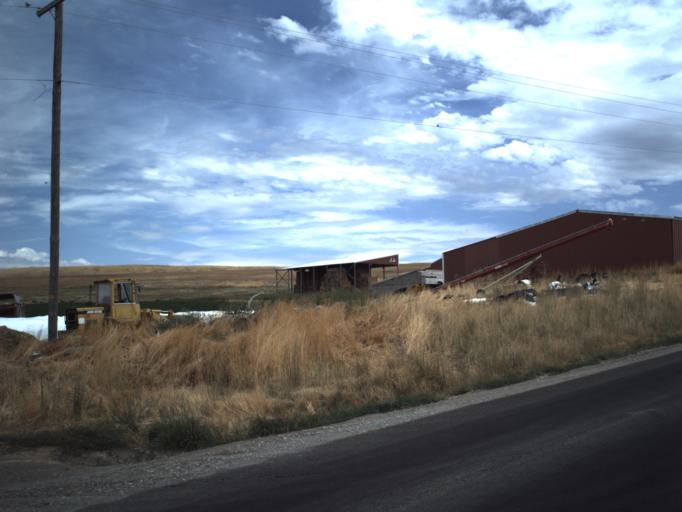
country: US
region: Utah
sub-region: Cache County
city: Benson
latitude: 41.8627
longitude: -111.9733
